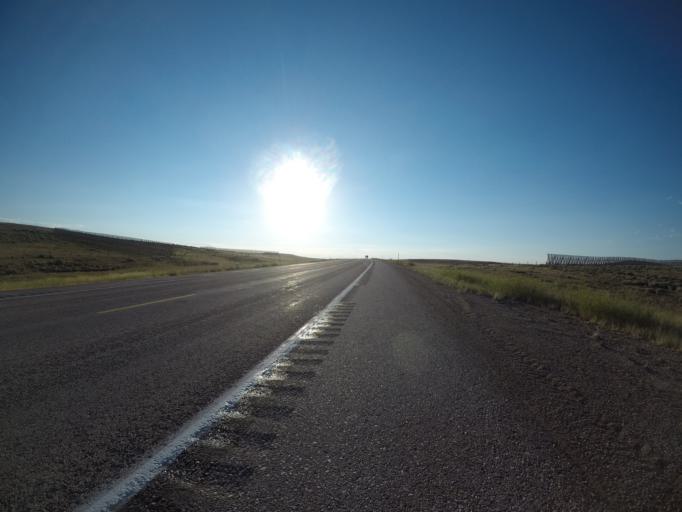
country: US
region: Wyoming
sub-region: Lincoln County
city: Kemmerer
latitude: 41.8679
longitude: -110.4645
